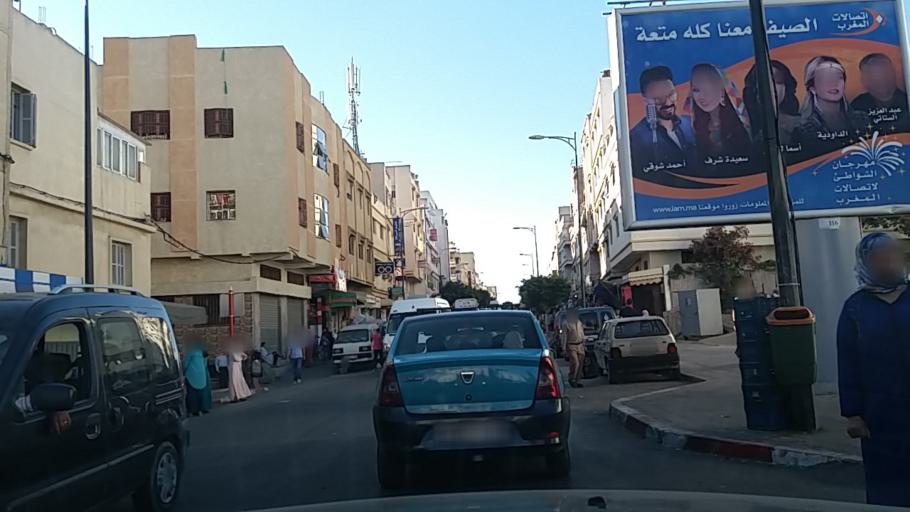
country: MA
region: Tanger-Tetouan
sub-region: Tanger-Assilah
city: Tangier
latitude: 35.7538
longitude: -5.8202
